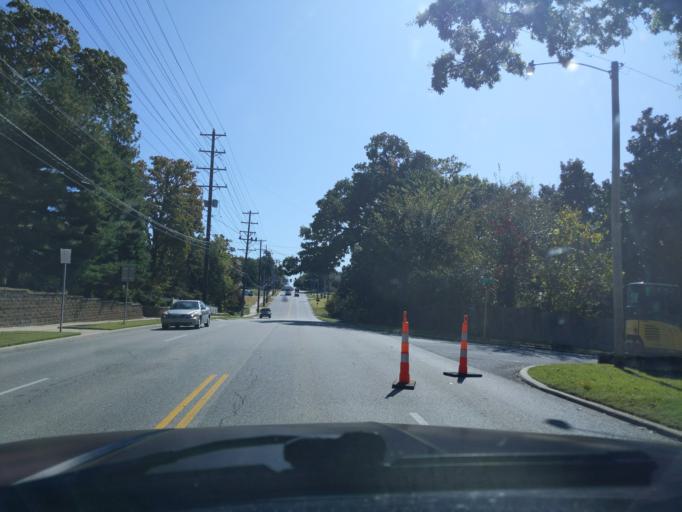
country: US
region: Oklahoma
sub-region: Tulsa County
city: Tulsa
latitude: 36.1133
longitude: -95.9581
